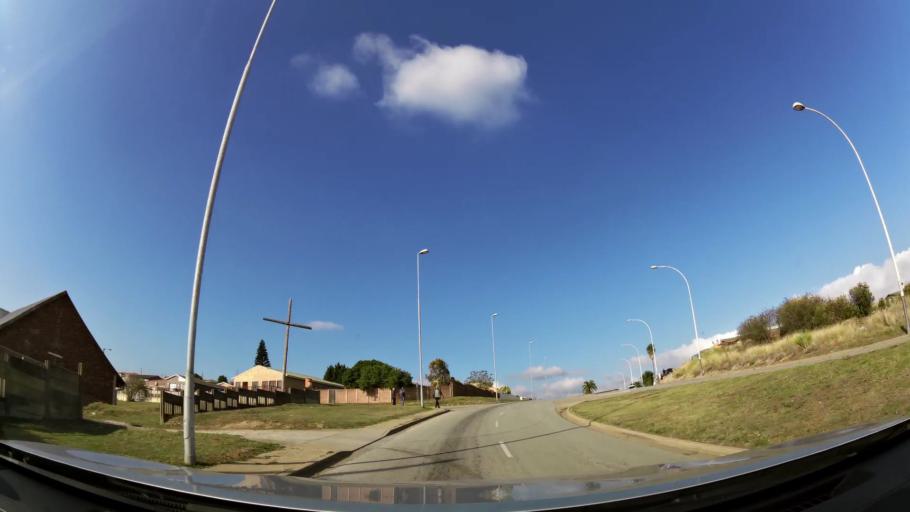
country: ZA
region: Eastern Cape
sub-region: Nelson Mandela Bay Metropolitan Municipality
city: Uitenhage
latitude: -33.7697
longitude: 25.4204
